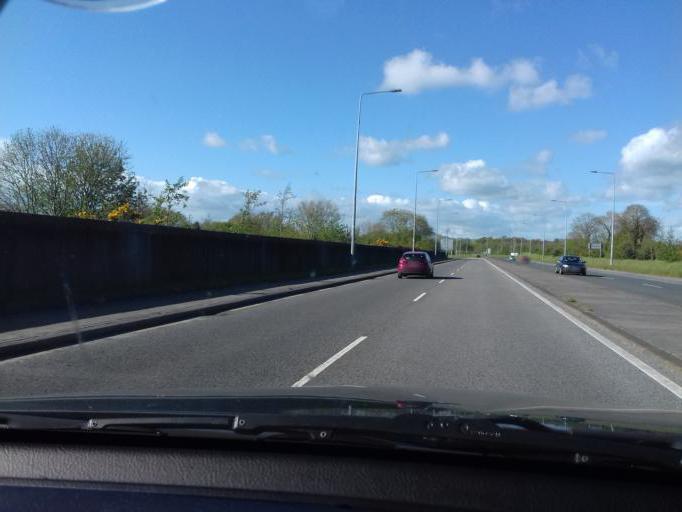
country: IE
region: Munster
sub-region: Waterford
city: Waterford
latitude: 52.2739
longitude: -7.1328
